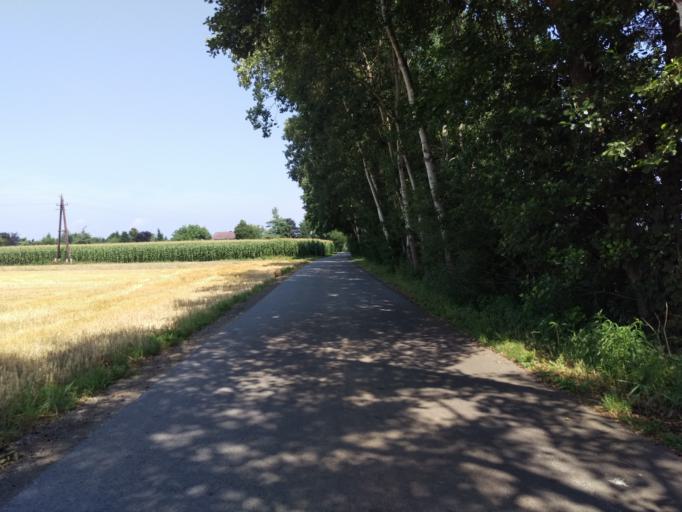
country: AT
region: Styria
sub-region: Politischer Bezirk Graz-Umgebung
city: Kalsdorf bei Graz
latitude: 46.9522
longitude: 15.4894
